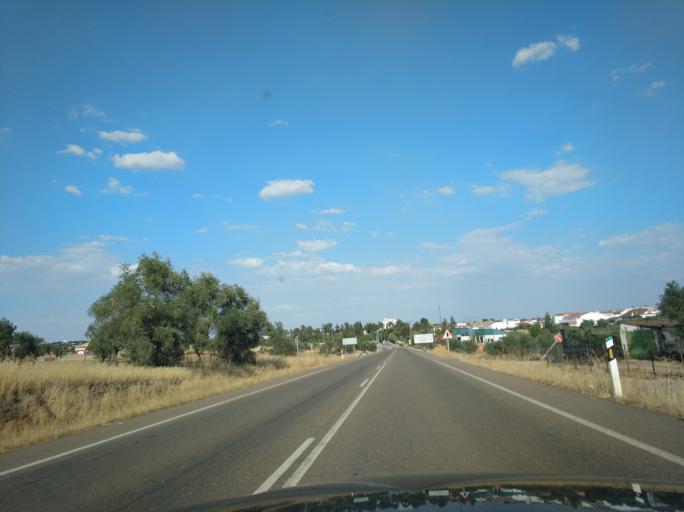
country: ES
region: Extremadura
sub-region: Provincia de Badajoz
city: Villanueva del Fresno
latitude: 38.3776
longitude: -7.1726
